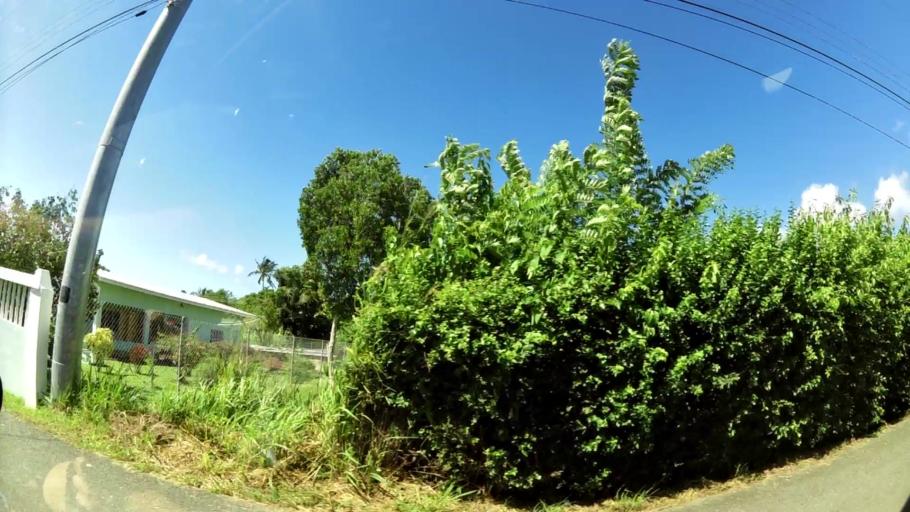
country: TT
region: Tobago
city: Scarborough
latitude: 11.1697
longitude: -60.7750
